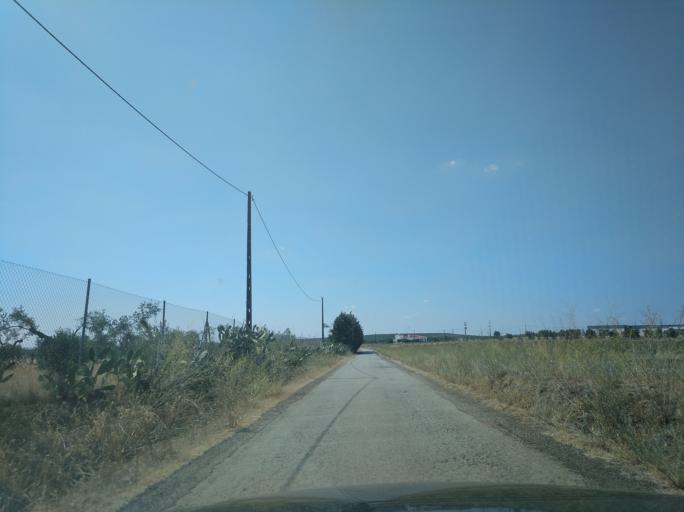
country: PT
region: Portalegre
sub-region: Campo Maior
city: Campo Maior
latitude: 39.0237
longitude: -7.0880
